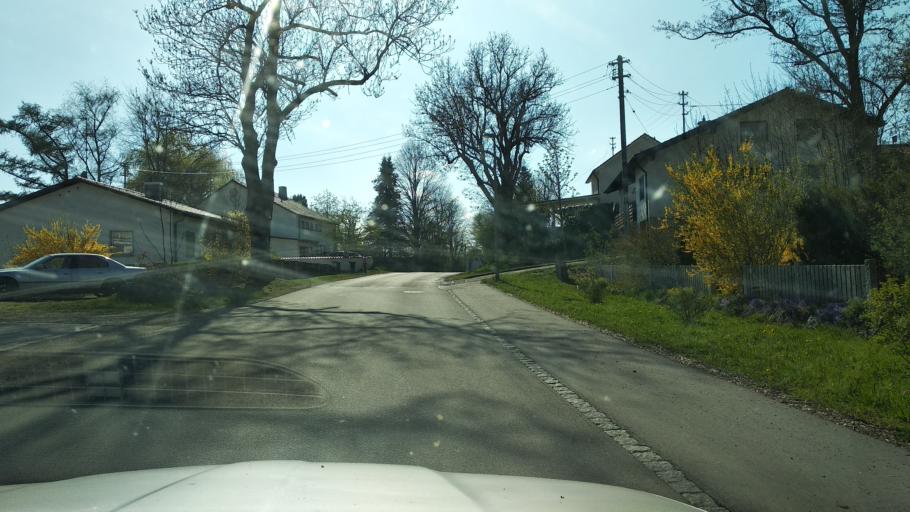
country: DE
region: Bavaria
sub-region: Swabia
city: Hawangen
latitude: 47.9718
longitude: 10.2754
